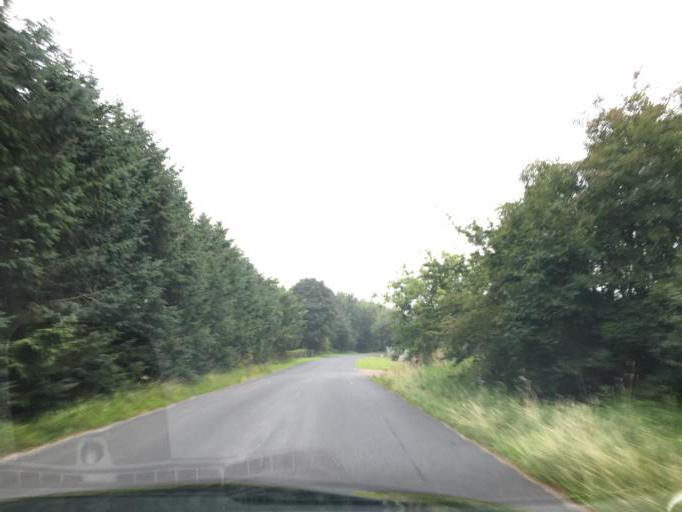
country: DK
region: South Denmark
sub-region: Kolding Kommune
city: Kolding
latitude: 55.5542
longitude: 9.4424
